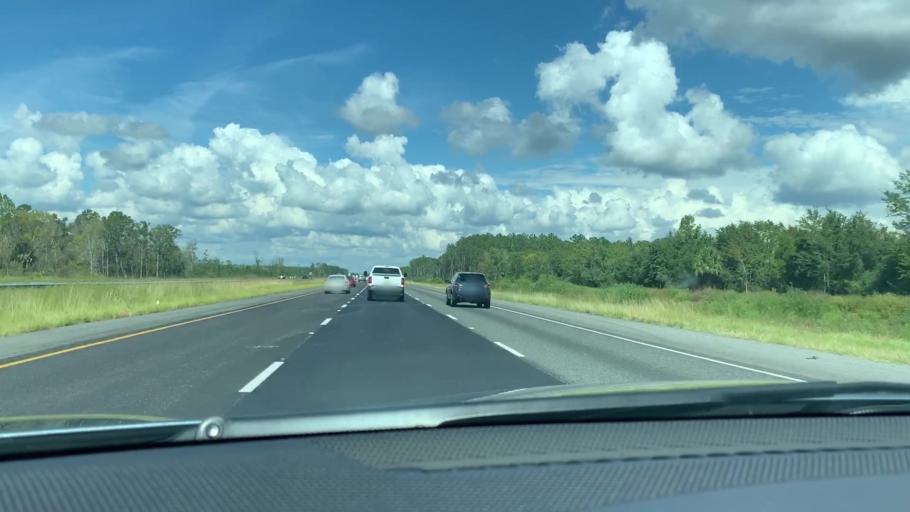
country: US
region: Georgia
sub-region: Camden County
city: Woodbine
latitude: 30.9932
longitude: -81.6652
